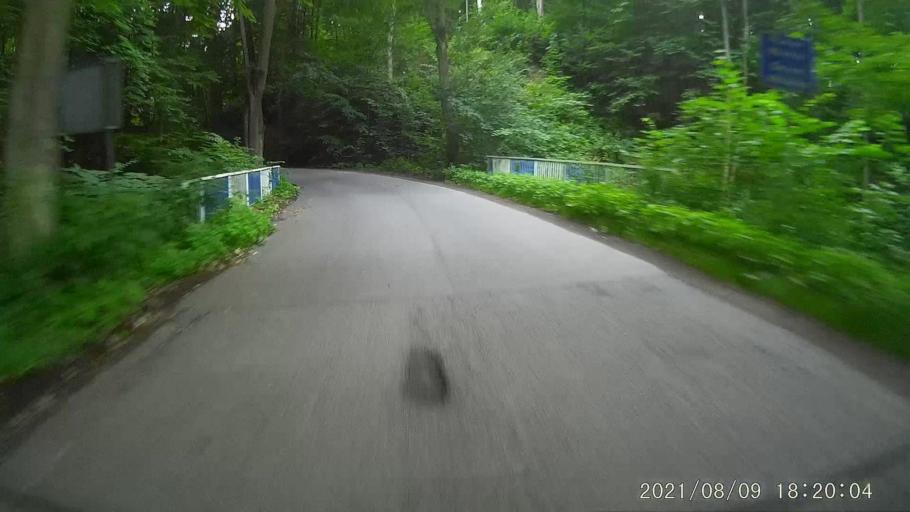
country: PL
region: Lower Silesian Voivodeship
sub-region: Powiat zabkowicki
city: Bardo
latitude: 50.5144
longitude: 16.6850
